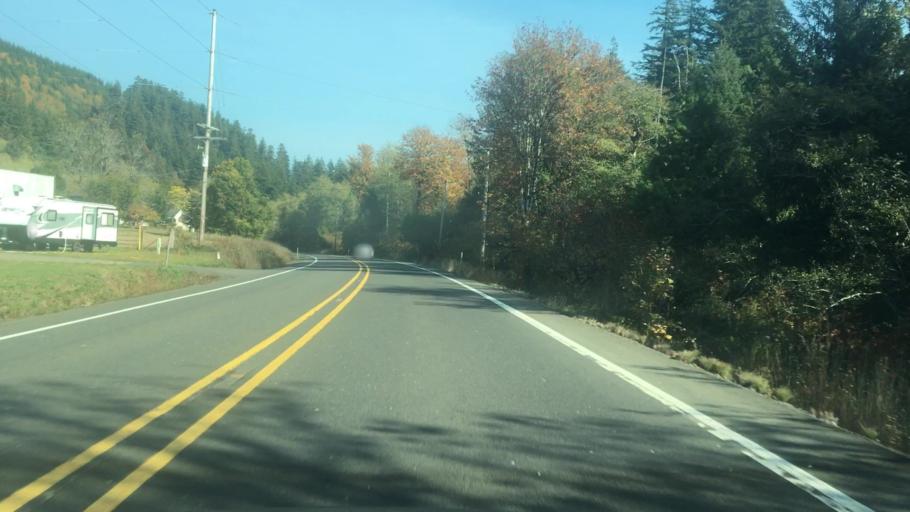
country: US
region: Oregon
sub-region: Lincoln County
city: Rose Lodge
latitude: 45.0228
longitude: -123.8308
